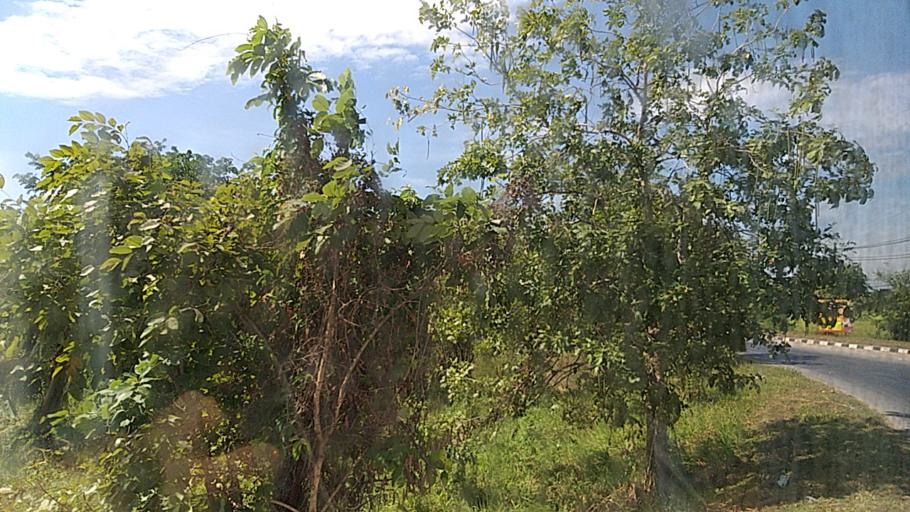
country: TH
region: Khon Kaen
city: Khon Kaen
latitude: 16.4401
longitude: 102.9175
